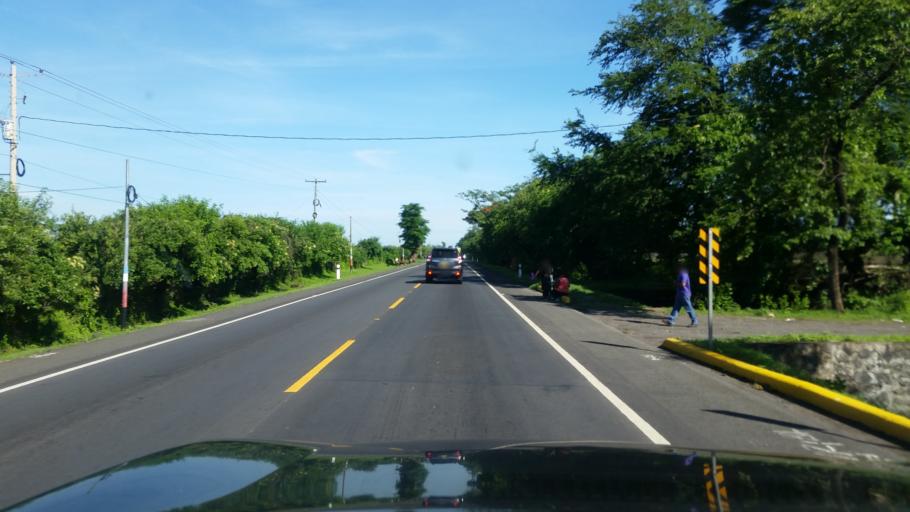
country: NI
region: Leon
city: Quezalguaque
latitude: 12.5410
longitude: -86.9135
